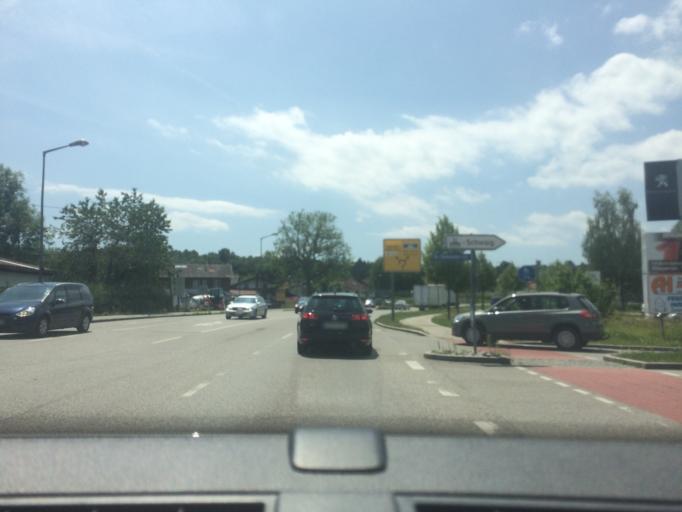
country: DE
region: Bavaria
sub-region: Upper Bavaria
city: Kolbermoor
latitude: 47.8432
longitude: 12.0877
